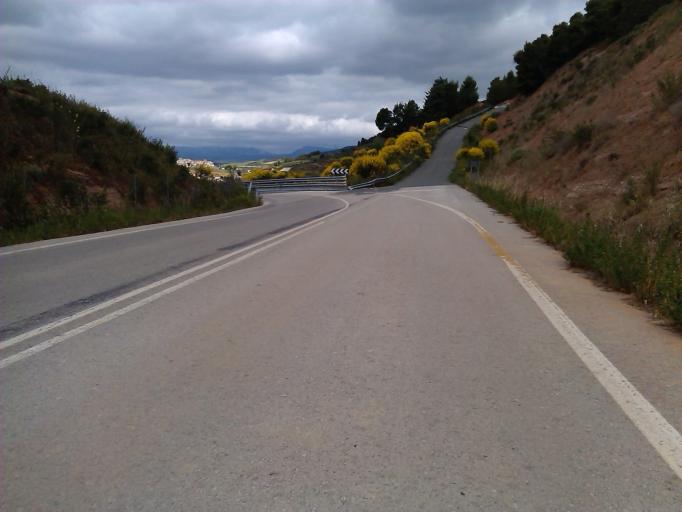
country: ES
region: Navarre
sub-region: Provincia de Navarra
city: Maneru
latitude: 42.6686
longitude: -1.8550
